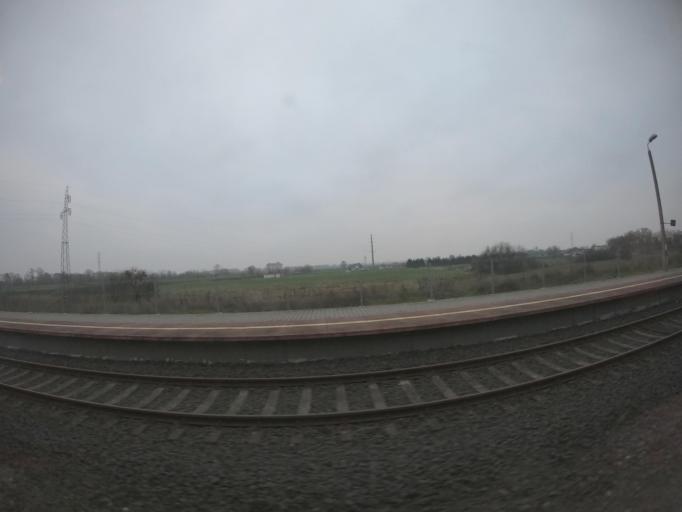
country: PL
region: Lubusz
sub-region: Powiat gorzowski
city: Jenin
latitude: 52.7018
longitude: 15.1272
